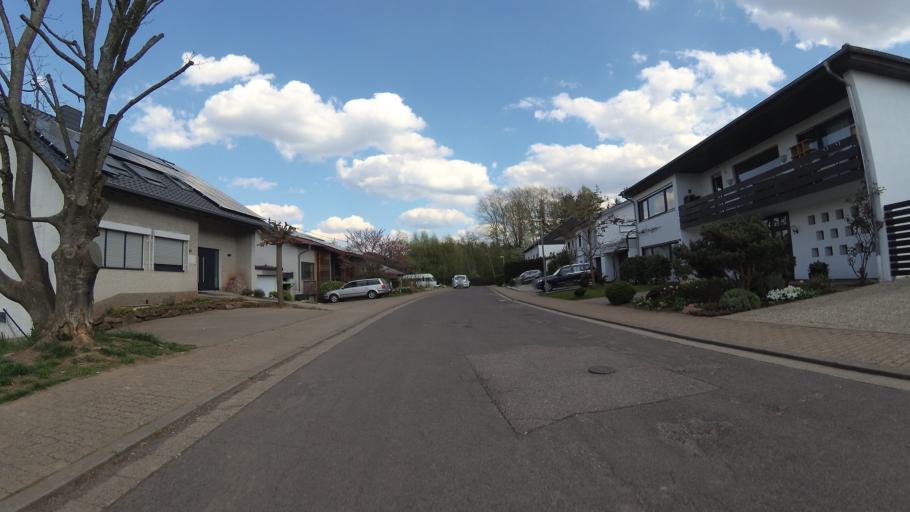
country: DE
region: Saarland
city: Riegelsberg
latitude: 49.2997
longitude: 6.9426
